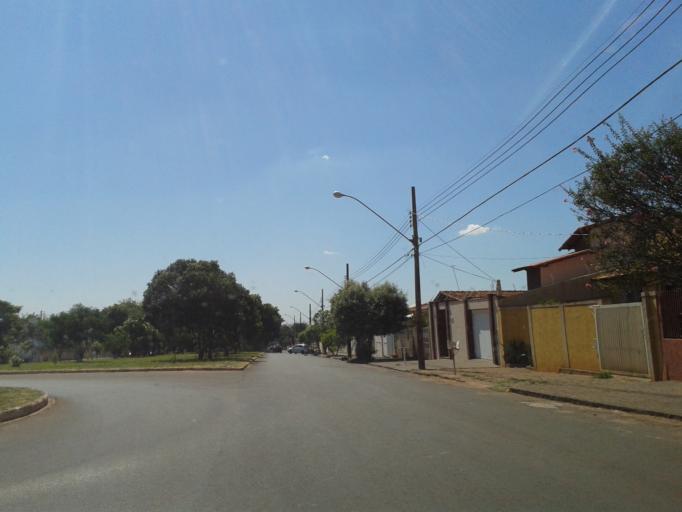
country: BR
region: Minas Gerais
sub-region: Ituiutaba
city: Ituiutaba
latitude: -18.9858
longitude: -49.4573
